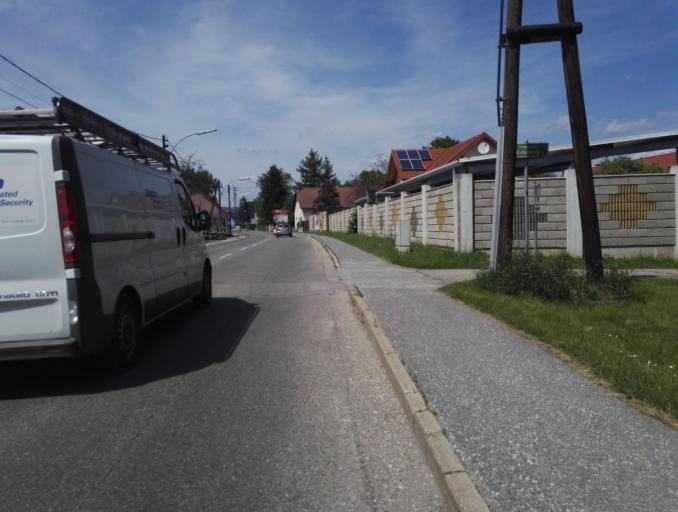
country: AT
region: Styria
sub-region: Politischer Bezirk Graz-Umgebung
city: Feldkirchen bei Graz
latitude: 47.0018
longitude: 15.4498
